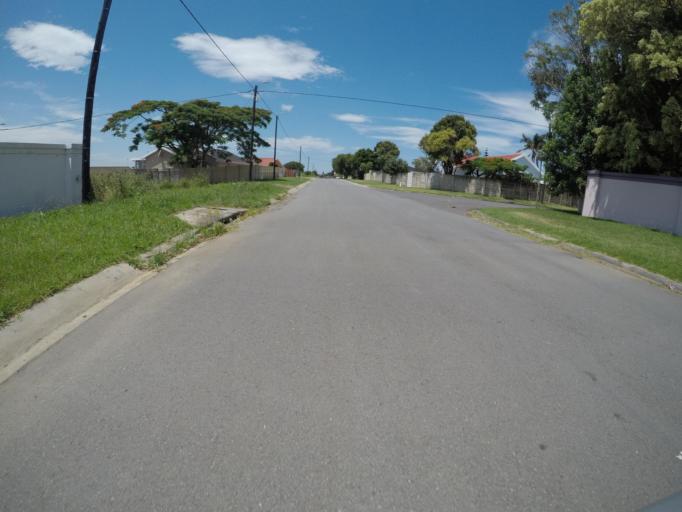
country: ZA
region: Eastern Cape
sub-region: Buffalo City Metropolitan Municipality
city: East London
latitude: -33.0322
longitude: 27.8515
